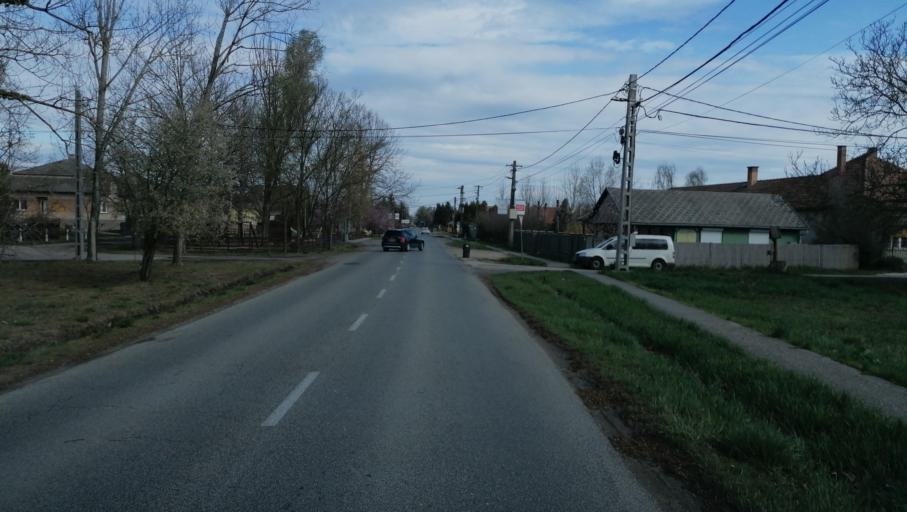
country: HU
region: Pest
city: Rackeve
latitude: 47.1417
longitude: 18.9474
